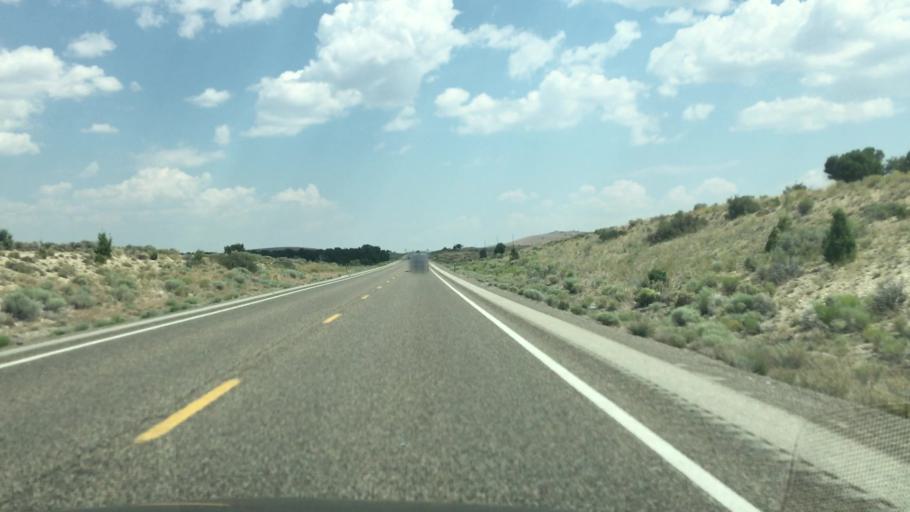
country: US
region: Nevada
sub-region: Elko County
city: Wells
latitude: 41.1996
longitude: -114.8606
